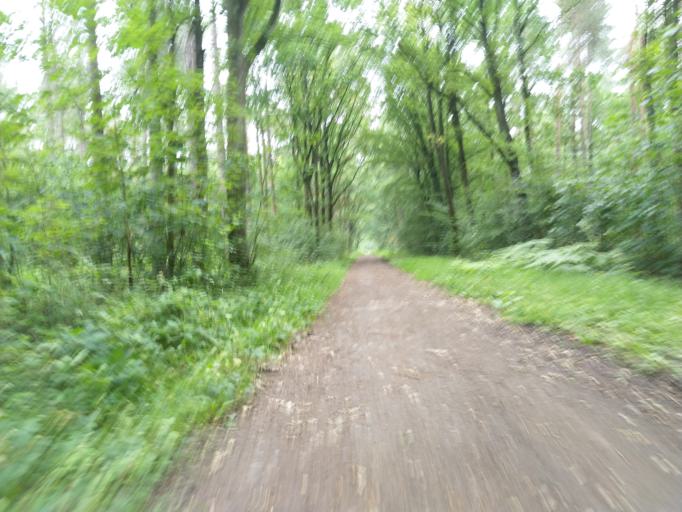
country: BE
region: Wallonia
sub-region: Province du Hainaut
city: Jurbise
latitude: 50.5007
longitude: 3.8736
